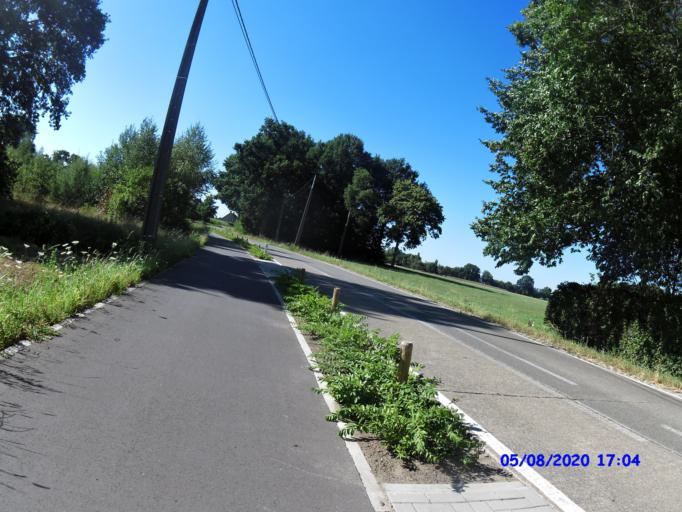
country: BE
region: Flanders
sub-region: Provincie Antwerpen
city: Oostmalle
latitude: 51.3082
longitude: 4.6858
